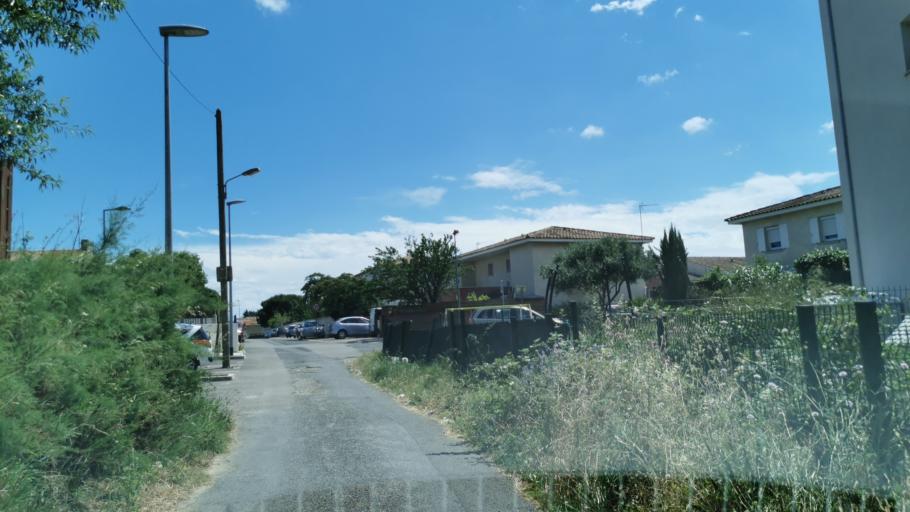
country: FR
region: Languedoc-Roussillon
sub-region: Departement de l'Aude
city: Narbonne
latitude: 43.1898
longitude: 2.9784
